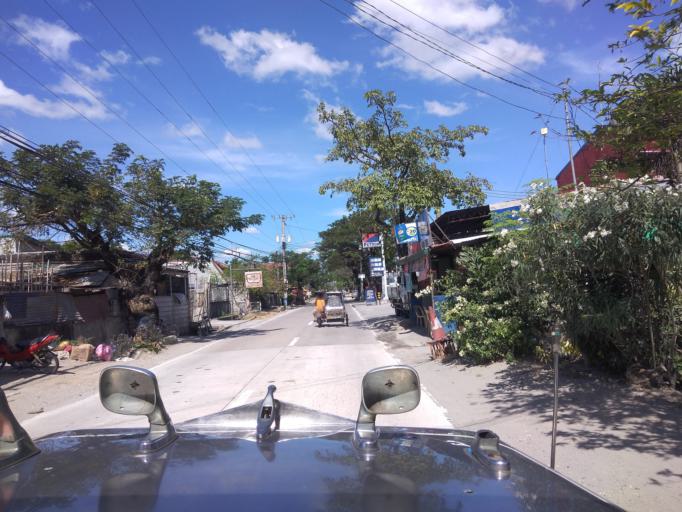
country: PH
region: Central Luzon
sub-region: Province of Pampanga
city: Santa Rita
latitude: 15.0002
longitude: 120.6112
